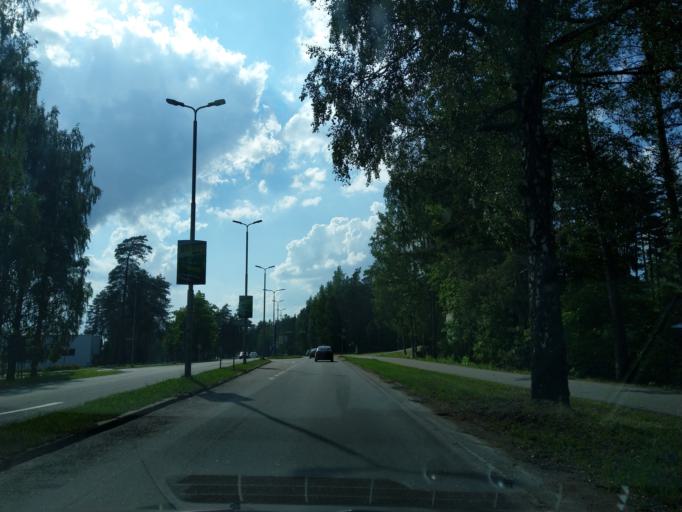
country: FI
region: Kymenlaakso
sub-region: Kouvola
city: Kouvola
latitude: 60.8776
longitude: 26.7500
